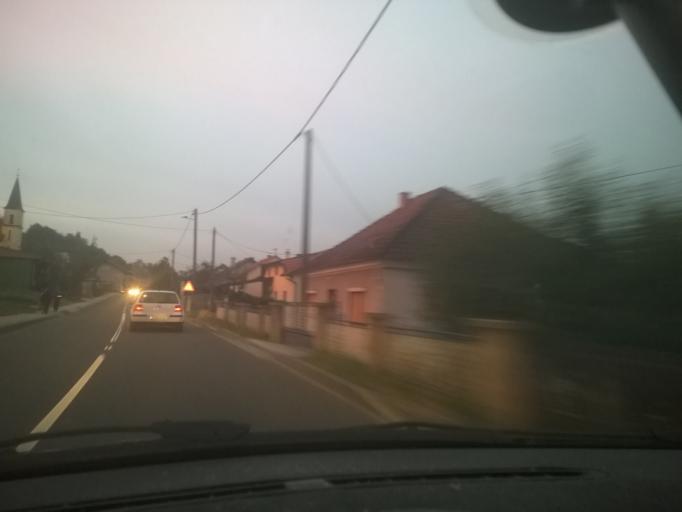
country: HR
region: Krapinsko-Zagorska
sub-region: Grad Krapina
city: Krapina
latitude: 46.1201
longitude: 15.8944
